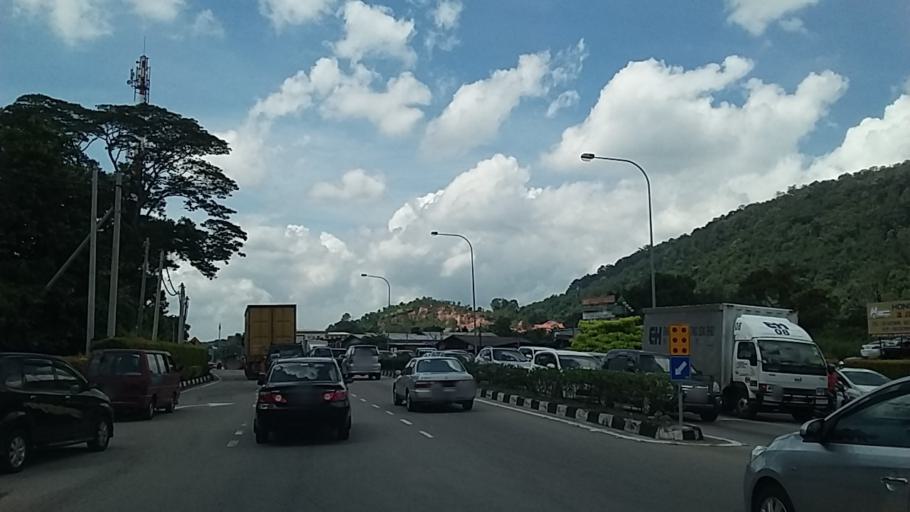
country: MY
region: Johor
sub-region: Daerah Batu Pahat
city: Batu Pahat
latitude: 1.8394
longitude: 102.9449
